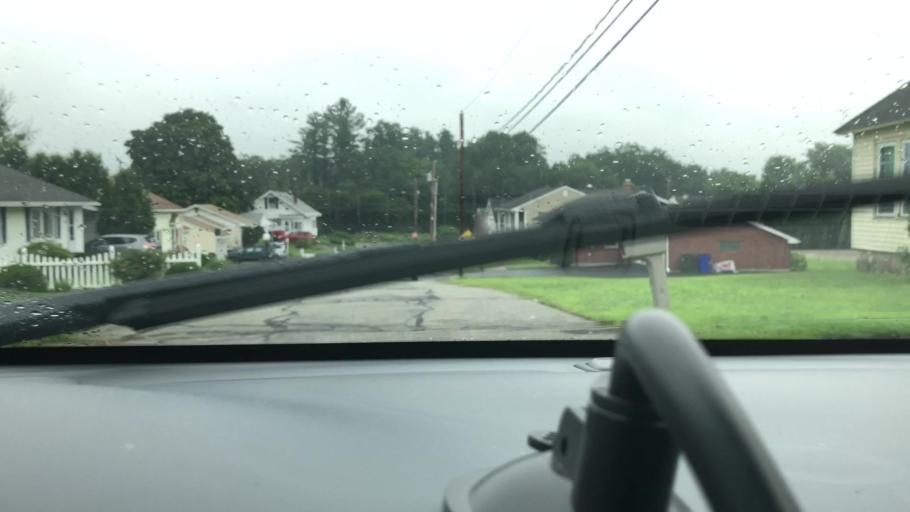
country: US
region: New Hampshire
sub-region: Hillsborough County
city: Pinardville
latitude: 42.9957
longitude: -71.5127
